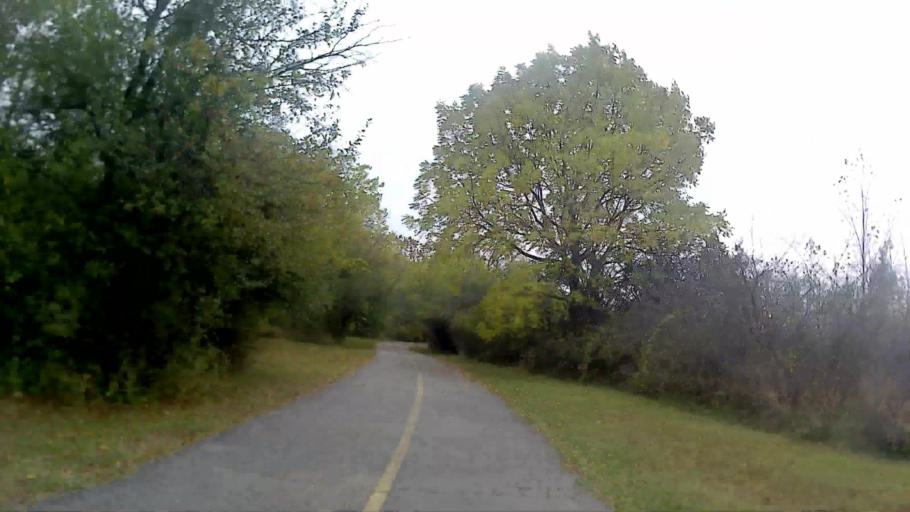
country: US
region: Illinois
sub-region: Kane County
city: Montgomery
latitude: 41.7571
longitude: -88.3838
